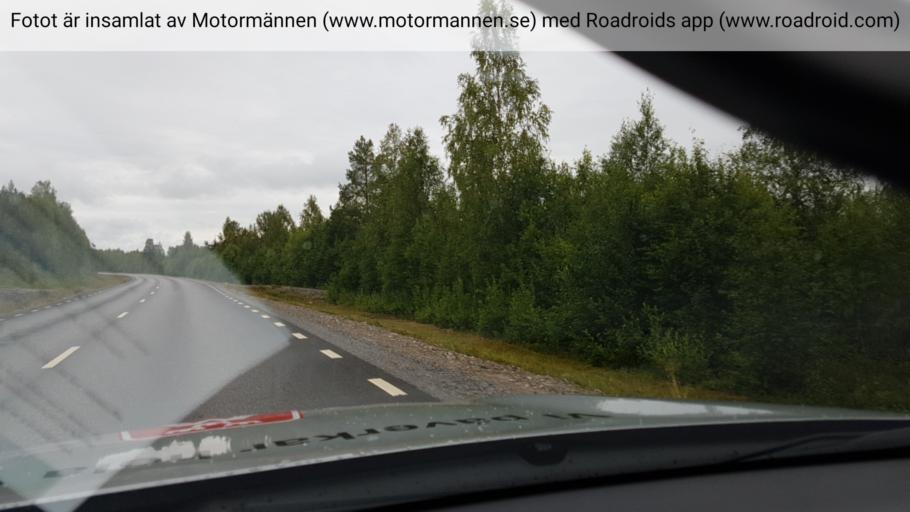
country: SE
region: Norrbotten
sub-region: Alvsbyns Kommun
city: AElvsbyn
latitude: 66.3110
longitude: 20.7971
